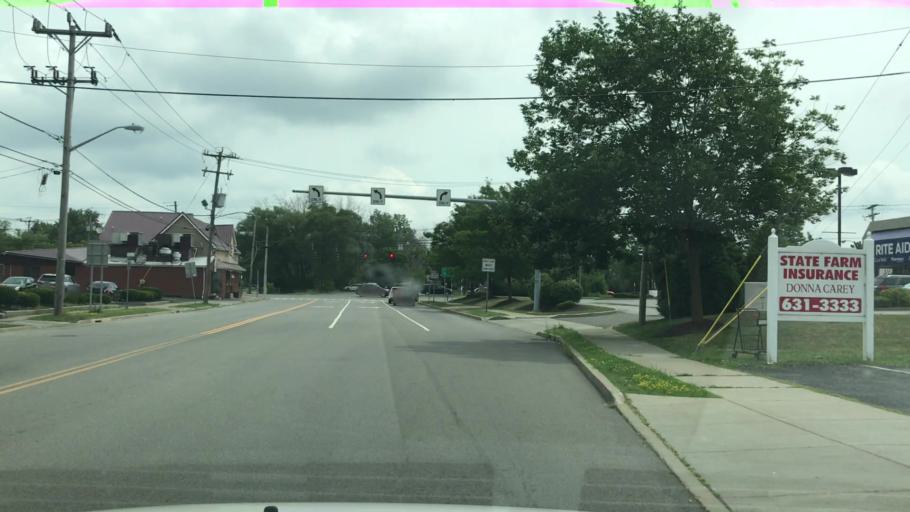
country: US
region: New York
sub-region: Erie County
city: Cheektowaga
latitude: 42.9219
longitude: -78.7555
